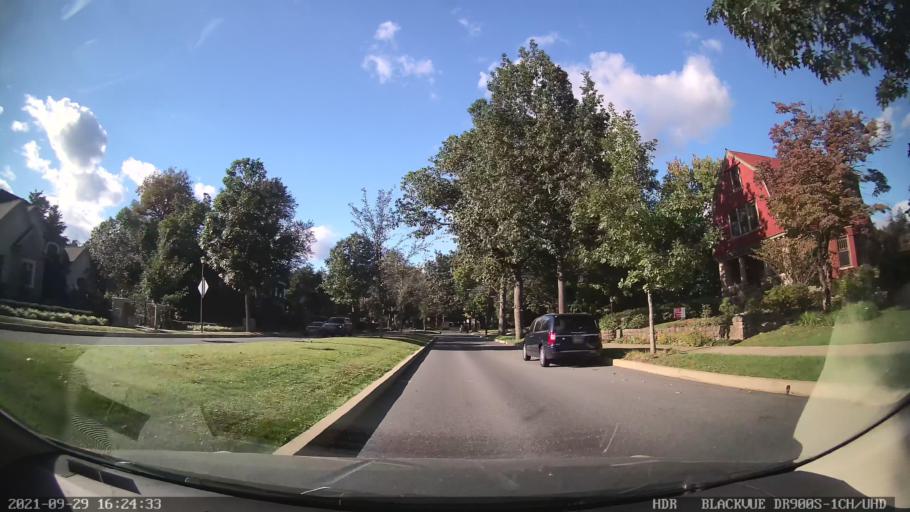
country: US
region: Pennsylvania
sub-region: Berks County
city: Wyomissing
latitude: 40.3333
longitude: -75.9580
